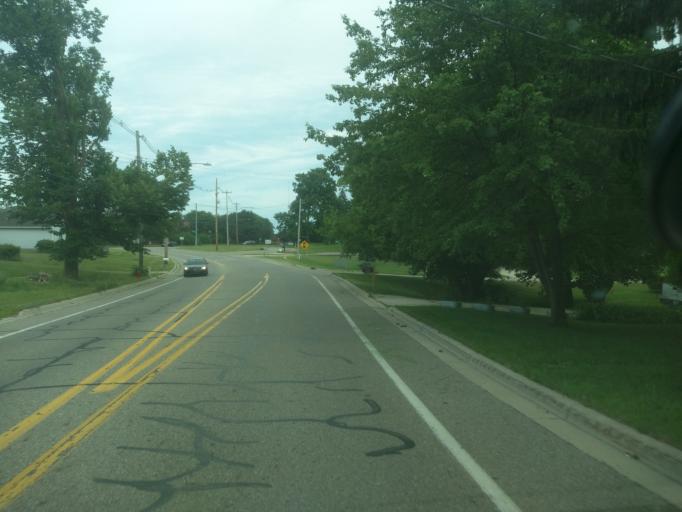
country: US
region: Michigan
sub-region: Ingham County
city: Holt
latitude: 42.6876
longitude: -84.5151
